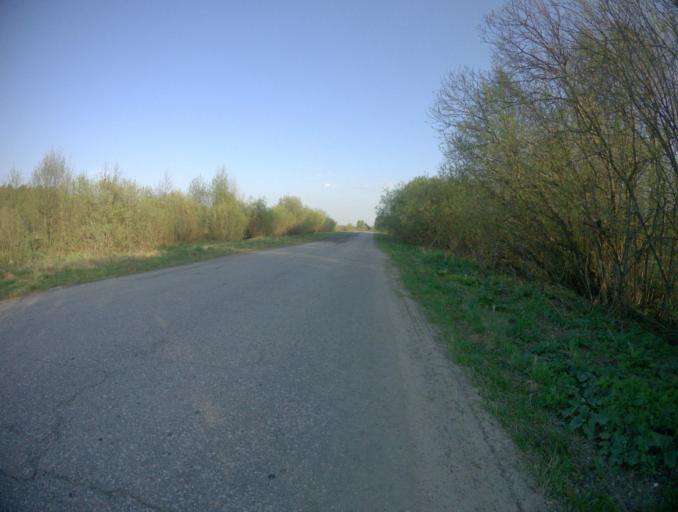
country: RU
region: Vladimir
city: Vyazniki
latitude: 56.3226
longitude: 42.1211
